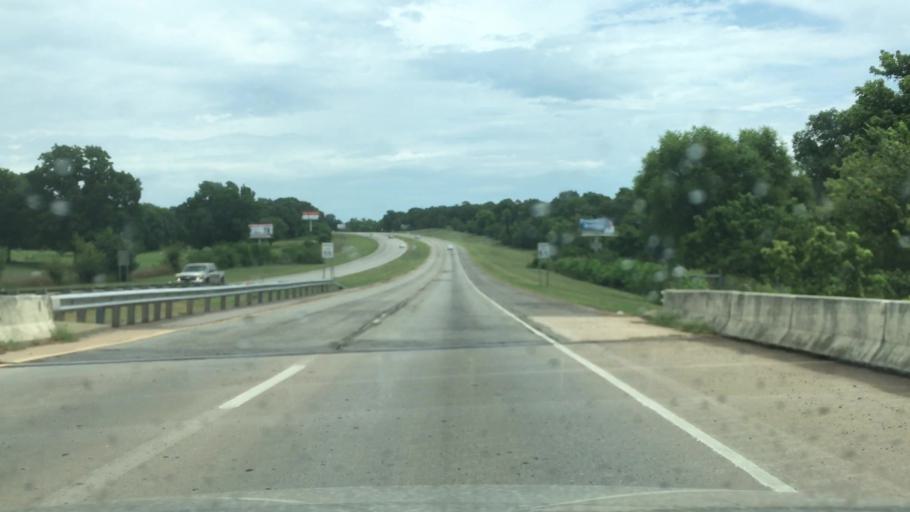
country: US
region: Oklahoma
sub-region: Cherokee County
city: Tahlequah
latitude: 35.8955
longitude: -94.9680
